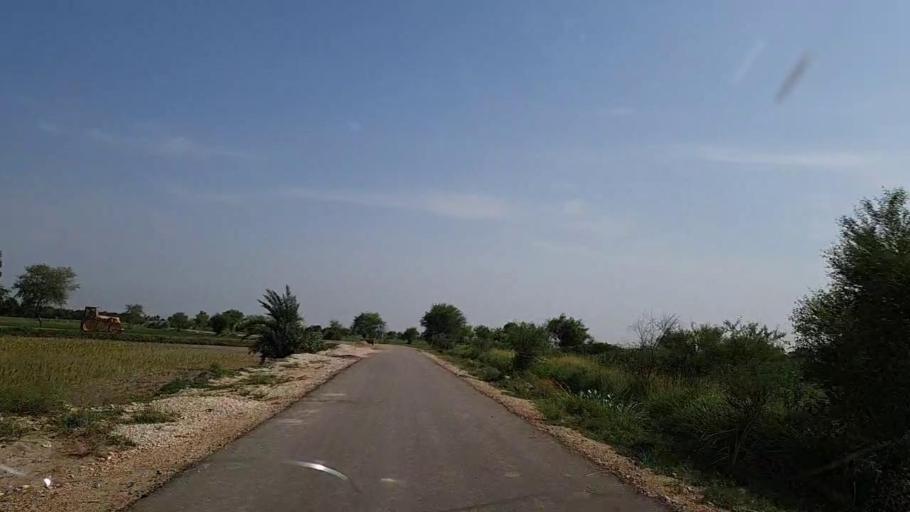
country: PK
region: Sindh
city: Khanpur
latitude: 27.6993
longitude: 69.3642
